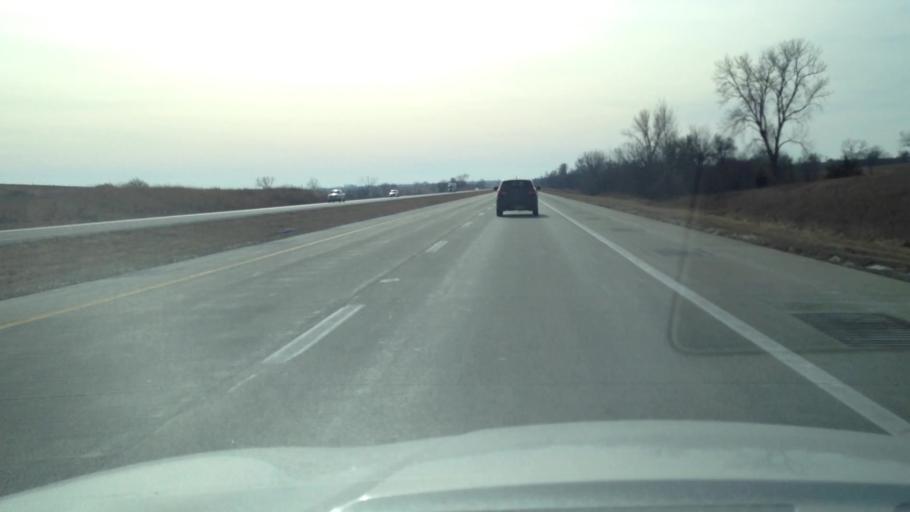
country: US
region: Missouri
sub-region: Harrison County
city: Bethany
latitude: 40.3376
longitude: -94.0115
